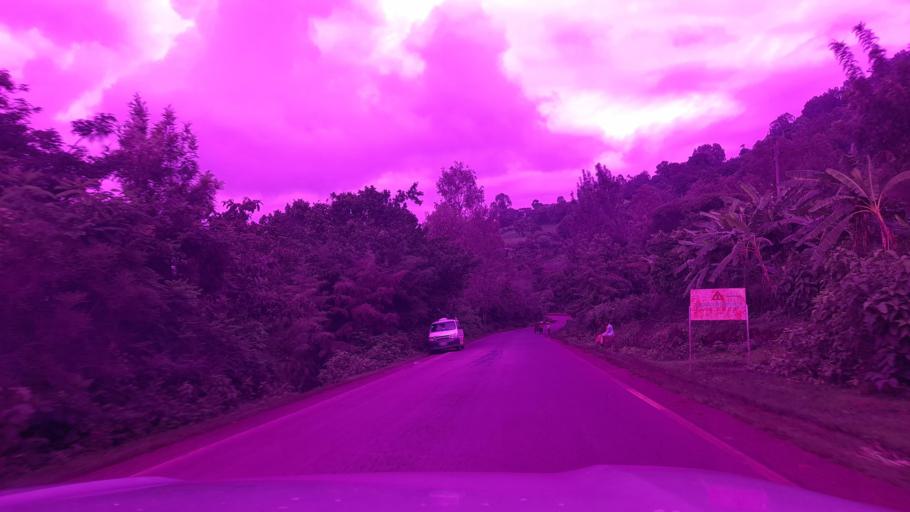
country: ET
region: Oromiya
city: Jima
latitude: 7.9111
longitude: 37.3963
